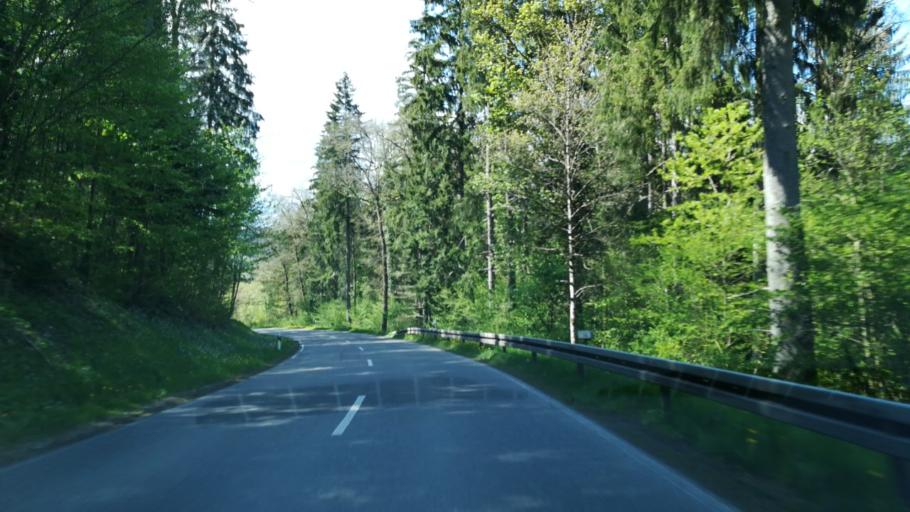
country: DE
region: Baden-Wuerttemberg
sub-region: Freiburg Region
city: Blumberg
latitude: 47.8456
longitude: 8.4559
